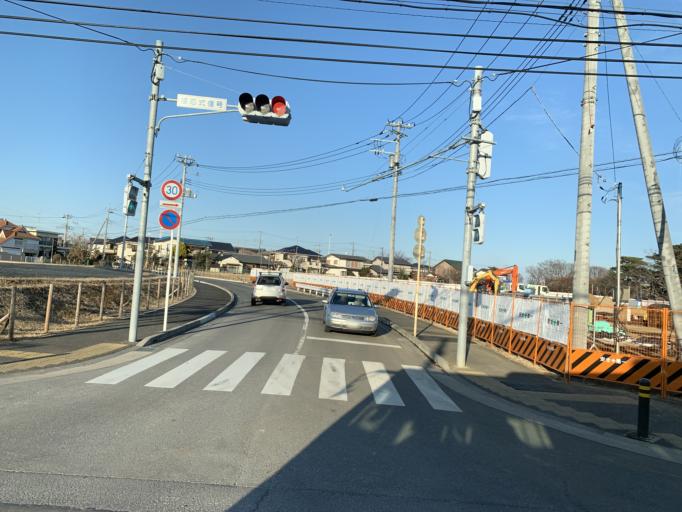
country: JP
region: Chiba
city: Kashiwa
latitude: 35.8668
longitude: 139.9585
